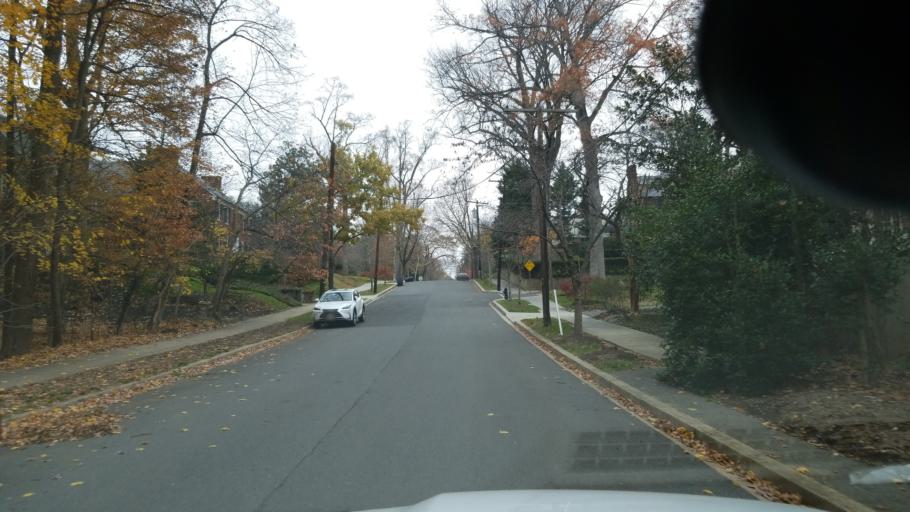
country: US
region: Maryland
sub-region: Montgomery County
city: Friendship Village
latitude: 38.9262
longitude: -77.0862
